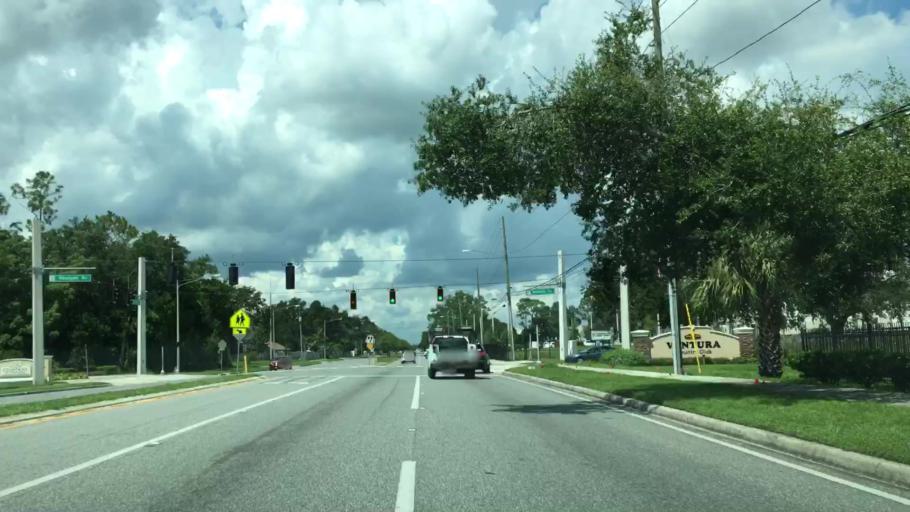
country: US
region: Florida
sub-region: Orange County
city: Conway
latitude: 28.4991
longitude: -81.2961
